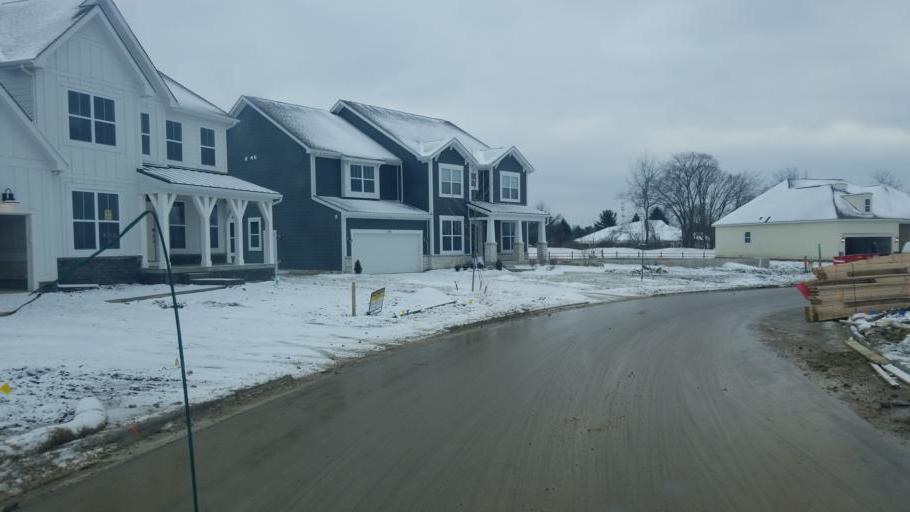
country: US
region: Ohio
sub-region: Franklin County
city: New Albany
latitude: 40.0358
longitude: -82.8153
